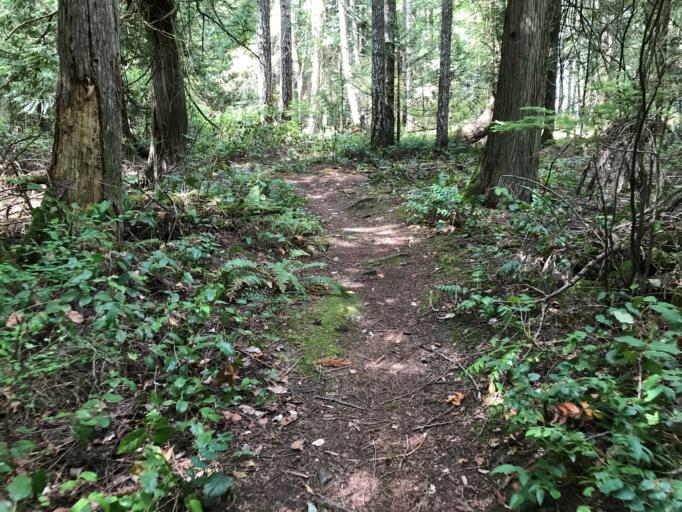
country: CA
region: British Columbia
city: North Cowichan
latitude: 48.9282
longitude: -123.7364
